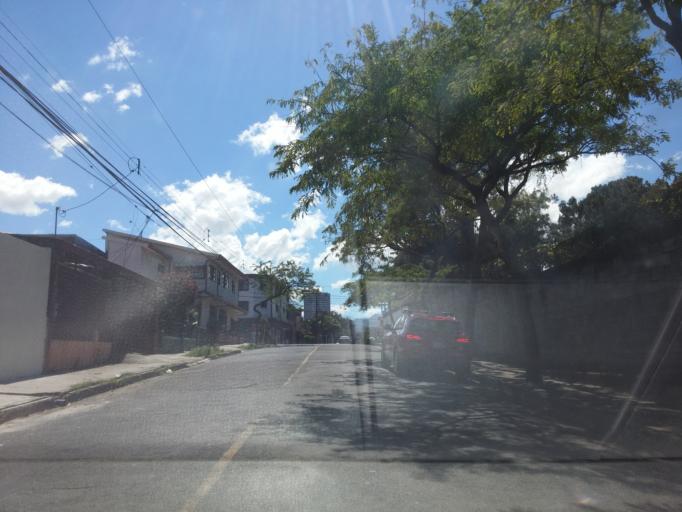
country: CR
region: San Jose
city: Colima
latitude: 9.9434
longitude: -84.0902
